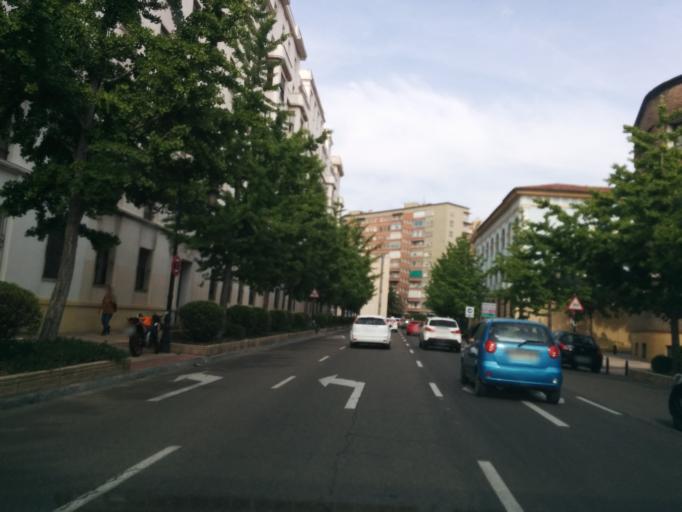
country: ES
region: Aragon
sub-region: Provincia de Zaragoza
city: Almozara
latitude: 41.6520
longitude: -0.8933
